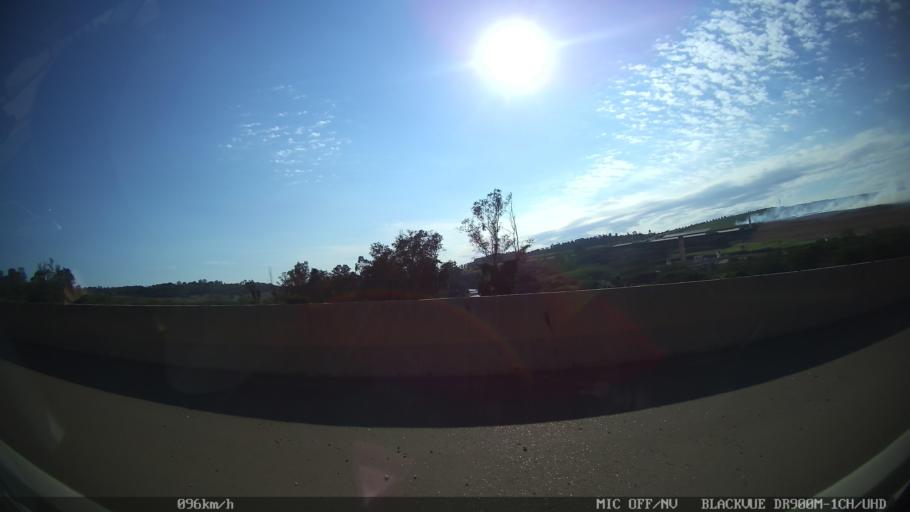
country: BR
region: Sao Paulo
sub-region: Piracicaba
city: Piracicaba
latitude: -22.7015
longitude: -47.6098
